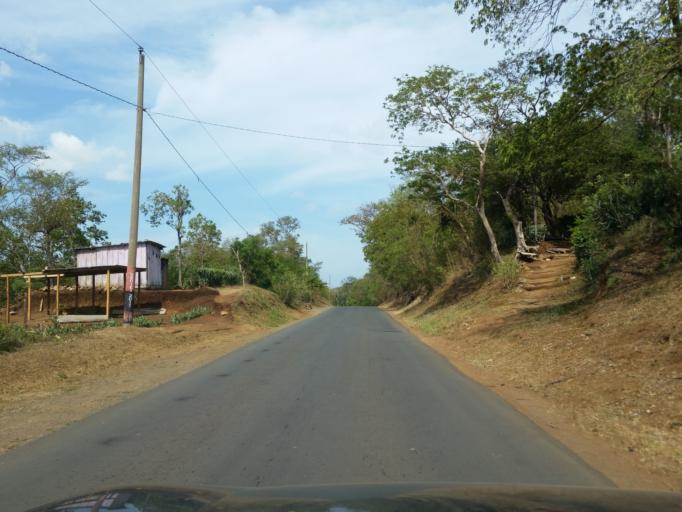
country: NI
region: Managua
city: San Rafael del Sur
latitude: 11.9097
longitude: -86.3799
